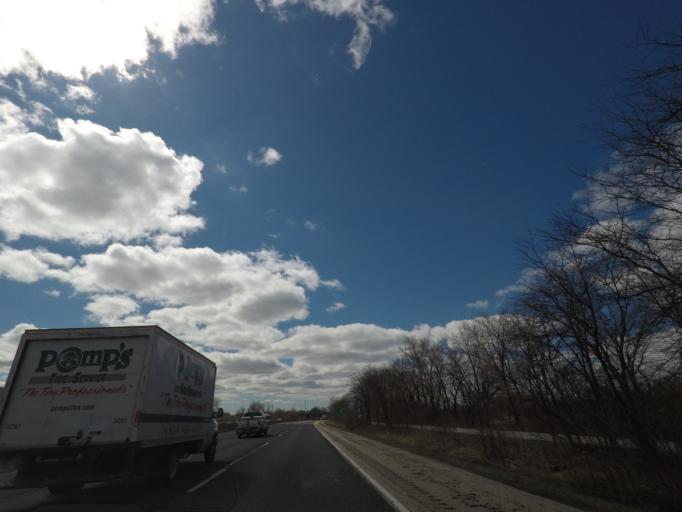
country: US
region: Illinois
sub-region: Will County
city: Shorewood
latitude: 41.5399
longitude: -88.1800
